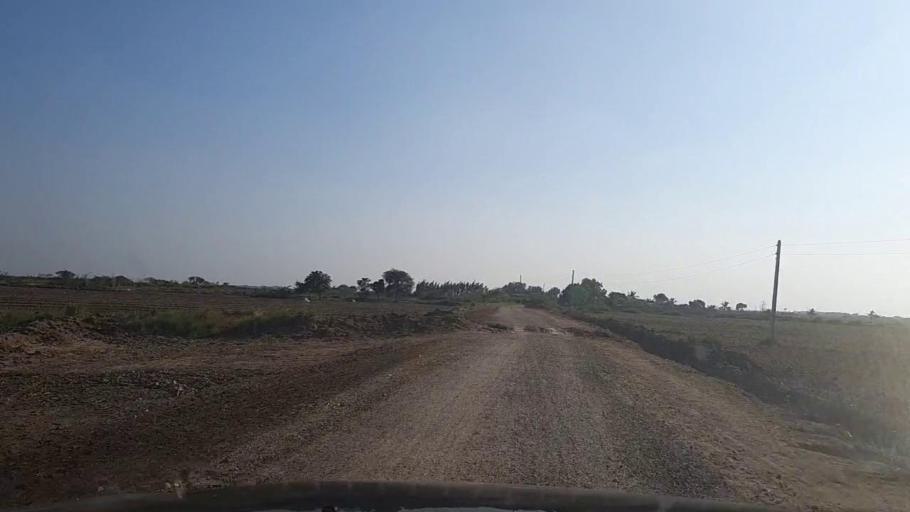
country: PK
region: Sindh
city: Gharo
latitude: 24.7072
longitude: 67.7044
